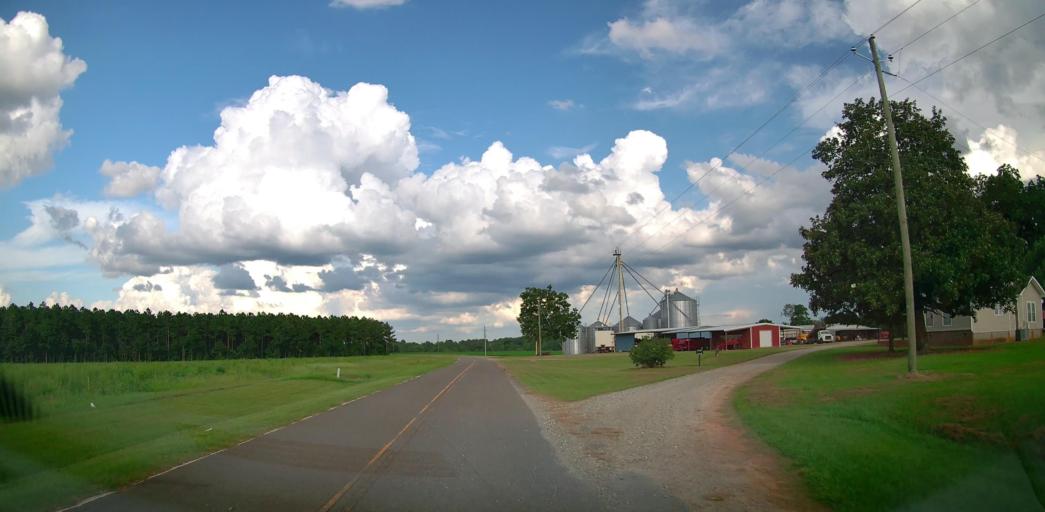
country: US
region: Georgia
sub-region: Bleckley County
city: Cochran
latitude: 32.4134
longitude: -83.4478
